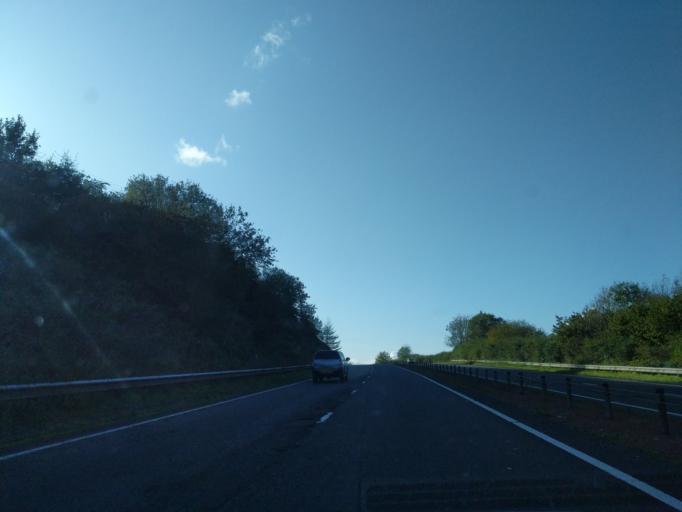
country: GB
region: Scotland
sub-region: Dumfries and Galloway
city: Dumfries
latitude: 55.0584
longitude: -3.7039
